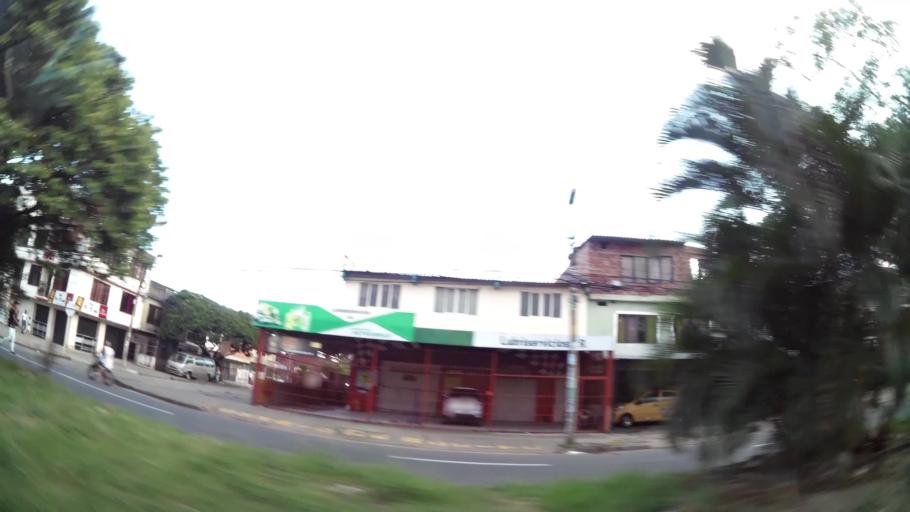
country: CO
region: Valle del Cauca
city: Cali
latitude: 3.4250
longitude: -76.5138
